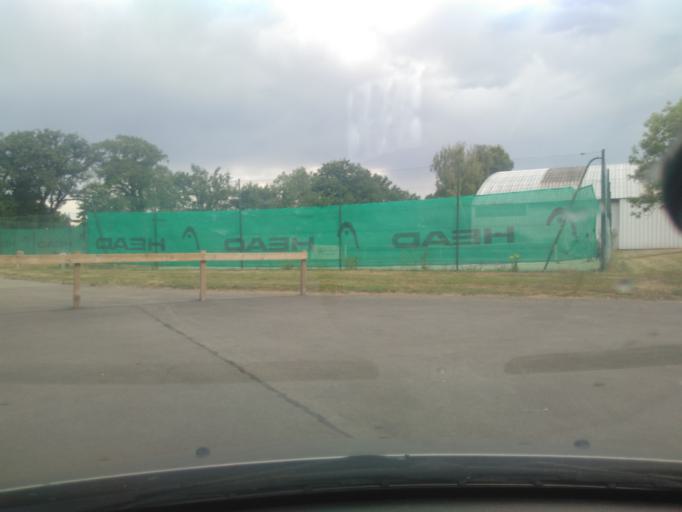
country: FR
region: Pays de la Loire
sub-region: Departement de la Vendee
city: Mouilleron-le-Captif
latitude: 46.6921
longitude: -1.4480
